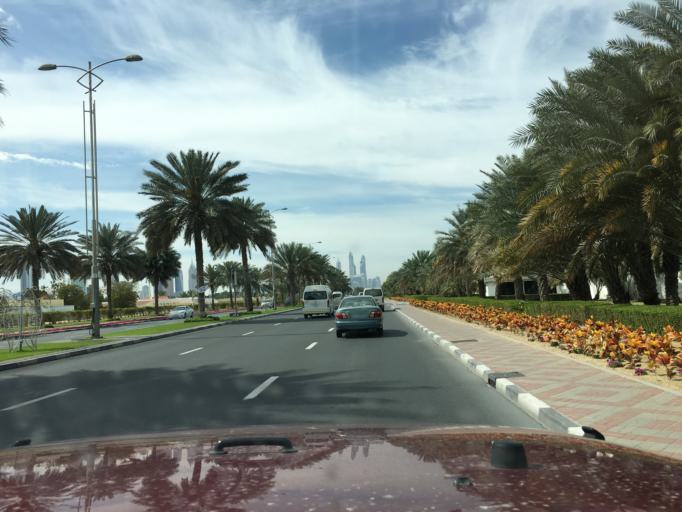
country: AE
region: Dubai
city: Dubai
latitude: 25.1266
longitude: 55.1824
